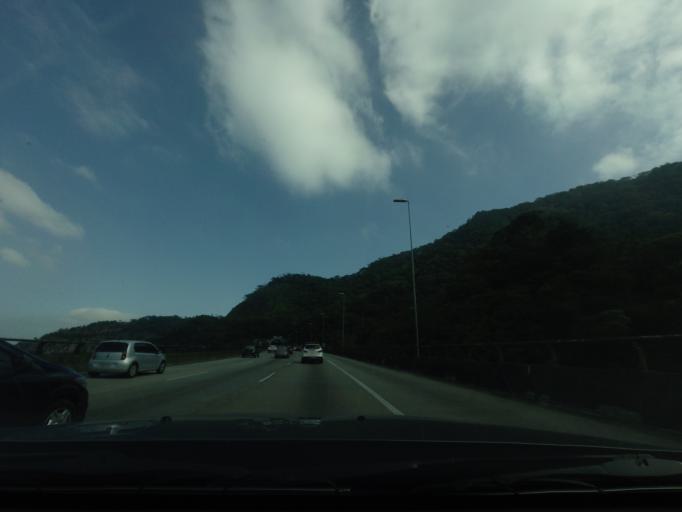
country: BR
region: Sao Paulo
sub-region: Cubatao
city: Cubatao
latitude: -23.8996
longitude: -46.5067
